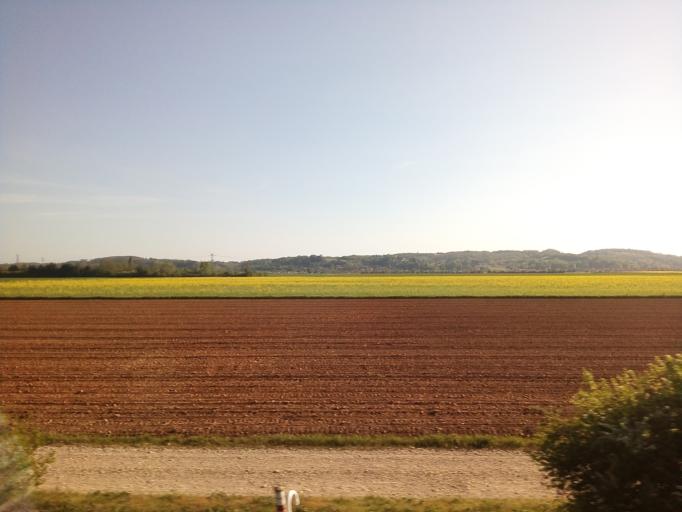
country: FR
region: Rhone-Alpes
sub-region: Departement du Rhone
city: Saint-Laurent-de-Mure
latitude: 45.6618
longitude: 5.0369
